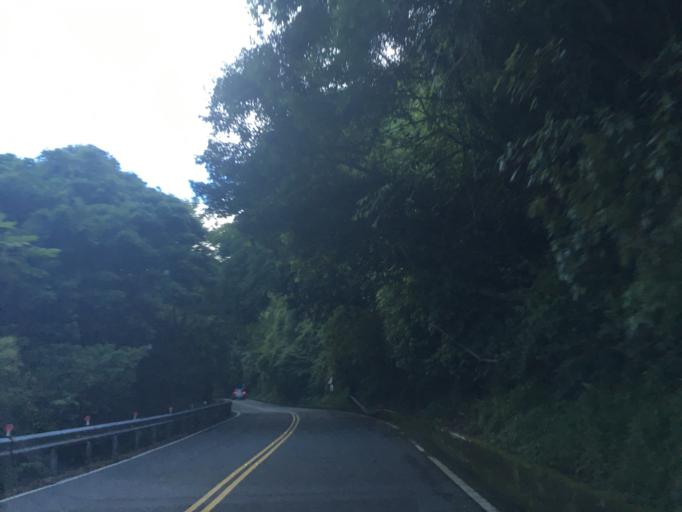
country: TW
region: Taiwan
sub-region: Nantou
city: Puli
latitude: 24.0791
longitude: 121.1686
